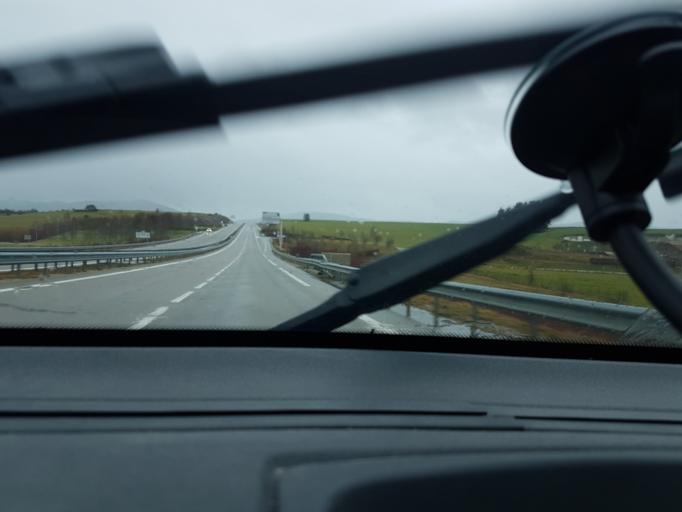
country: FR
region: Franche-Comte
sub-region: Departement du Doubs
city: Vercel-Villedieu-le-Camp
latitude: 47.1454
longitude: 6.4420
